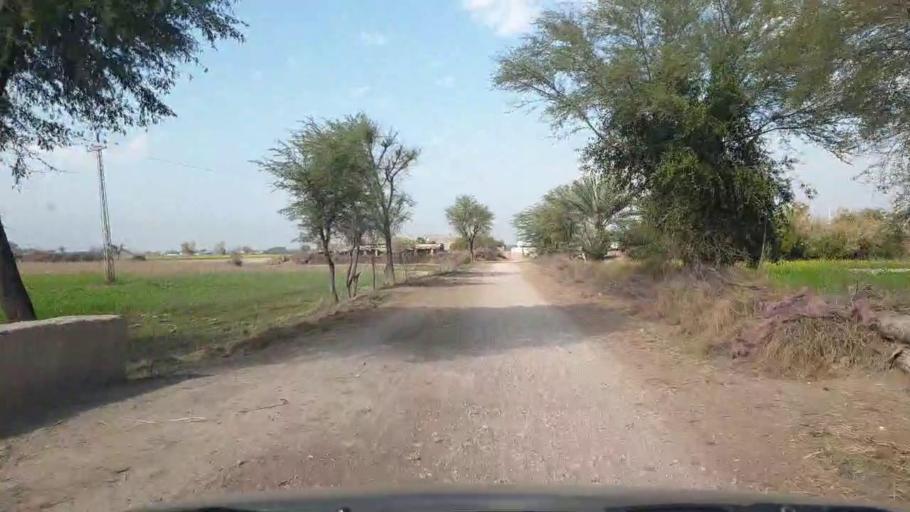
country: PK
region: Sindh
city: Sakrand
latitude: 26.0206
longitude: 68.4171
